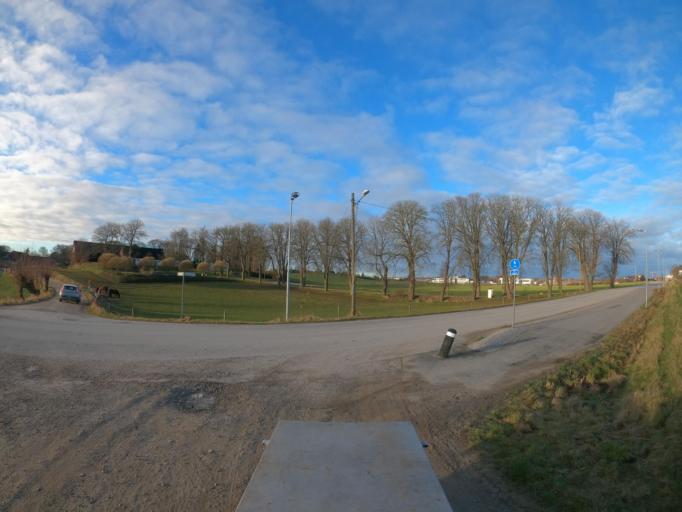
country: SE
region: Skane
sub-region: Svedala Kommun
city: Svedala
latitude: 55.4964
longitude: 13.2374
